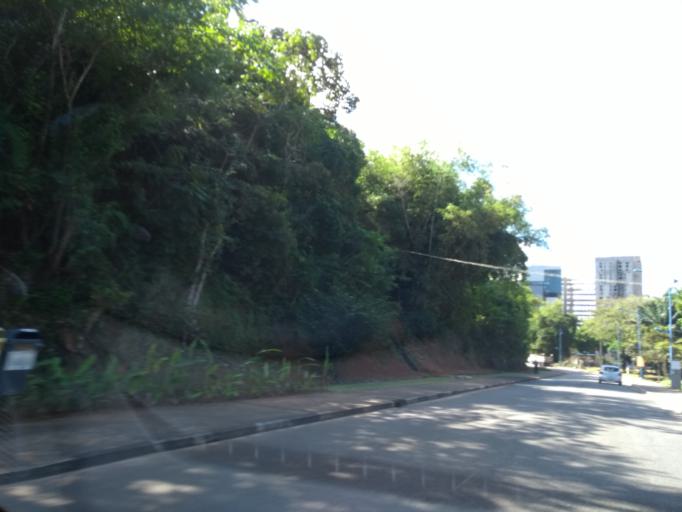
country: BR
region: Bahia
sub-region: Salvador
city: Salvador
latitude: -13.0050
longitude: -38.5113
